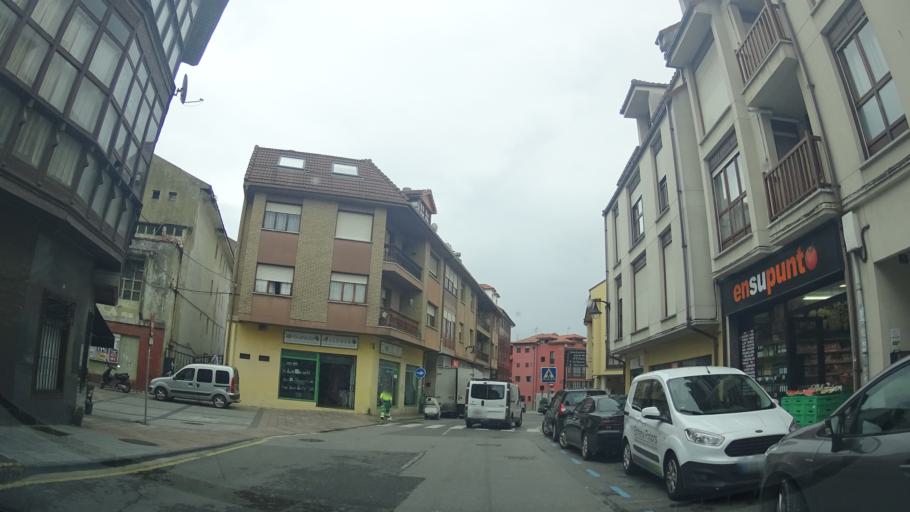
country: ES
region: Asturias
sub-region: Province of Asturias
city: Llanes
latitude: 43.4204
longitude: -4.7573
